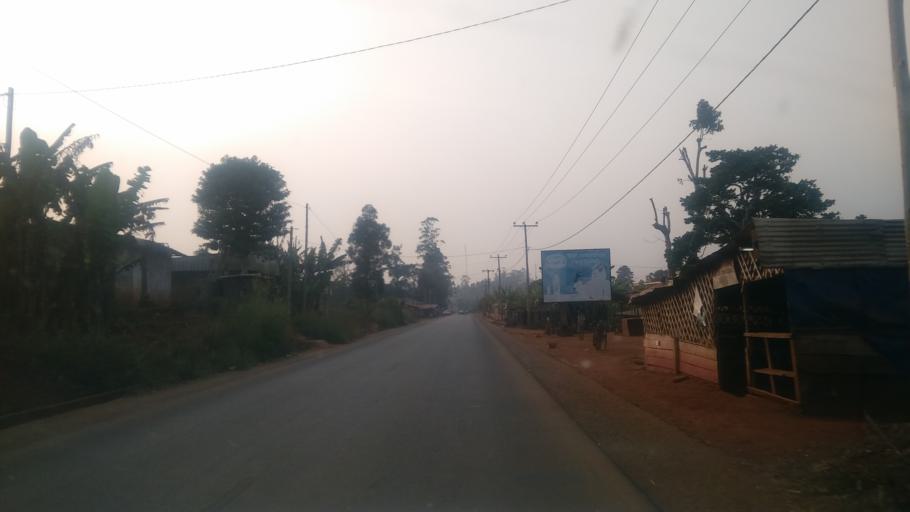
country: CM
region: West
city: Bana
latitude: 5.1396
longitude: 10.2814
